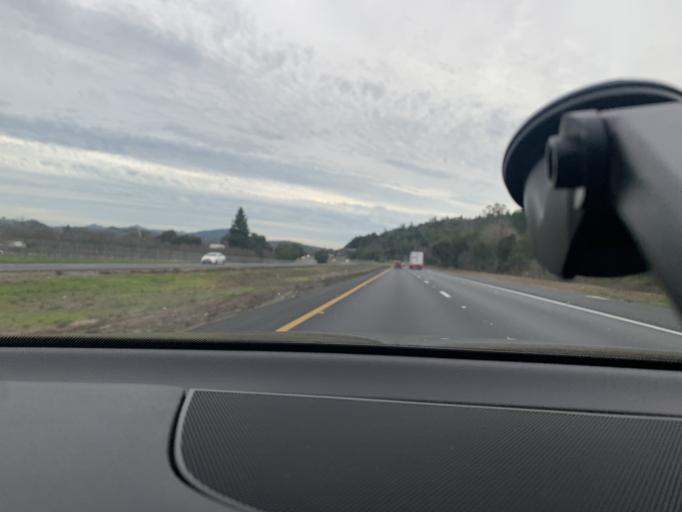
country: US
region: California
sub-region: Sonoma County
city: Healdsburg
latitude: 38.6739
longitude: -122.8806
